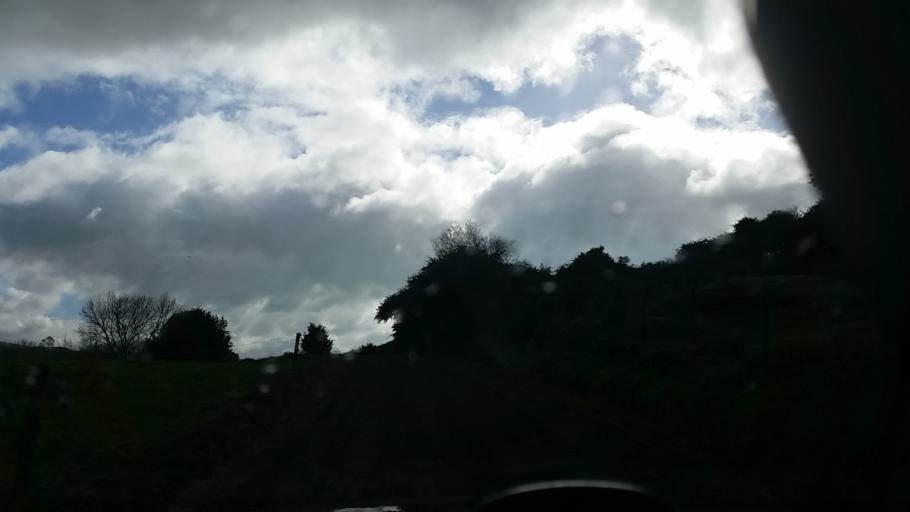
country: NZ
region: Waikato
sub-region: Matamata-Piako District
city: Matamata
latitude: -37.8103
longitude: 175.6730
